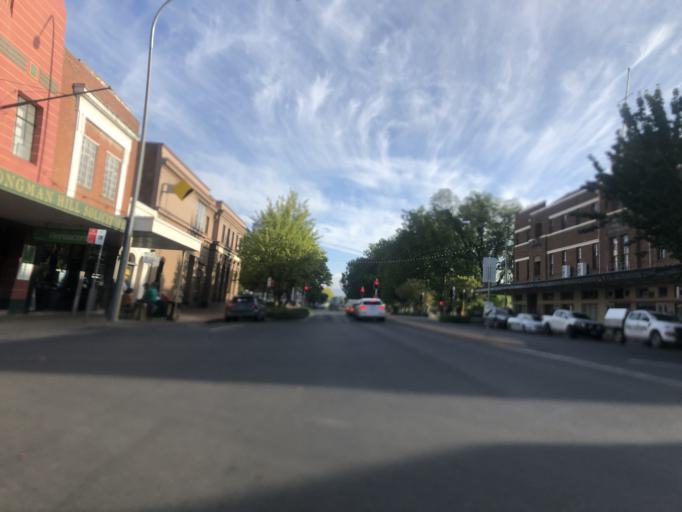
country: AU
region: New South Wales
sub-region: Orange Municipality
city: Orange
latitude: -33.2845
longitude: 149.1009
